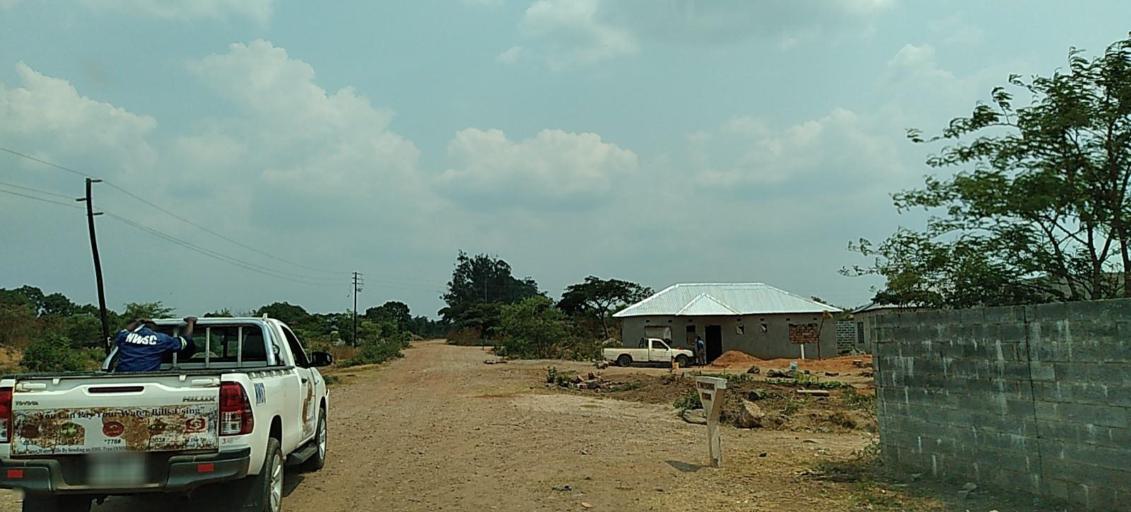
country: ZM
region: Copperbelt
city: Kalulushi
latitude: -12.8244
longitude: 28.0764
